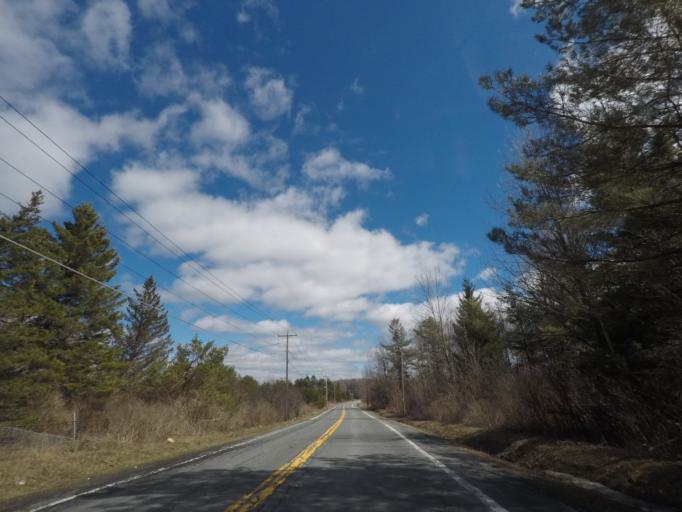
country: US
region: New York
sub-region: Albany County
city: Altamont
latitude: 42.6693
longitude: -74.0653
